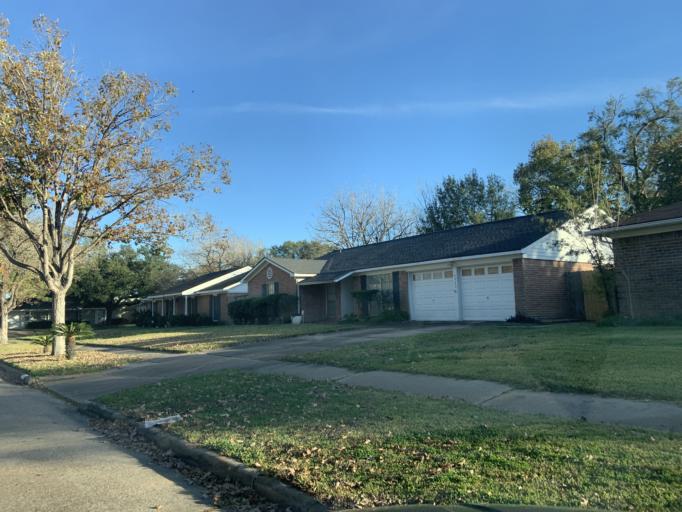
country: US
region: Texas
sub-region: Harris County
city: Bellaire
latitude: 29.6853
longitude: -95.5192
